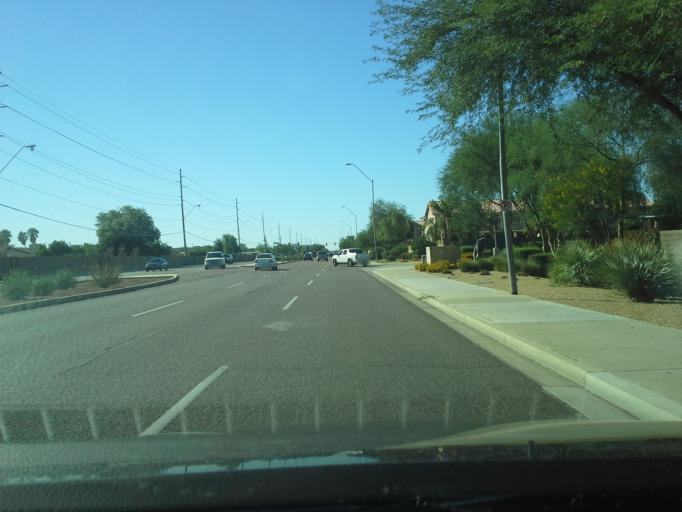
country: US
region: Arizona
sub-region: Maricopa County
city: Paradise Valley
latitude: 33.6407
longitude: -111.9831
